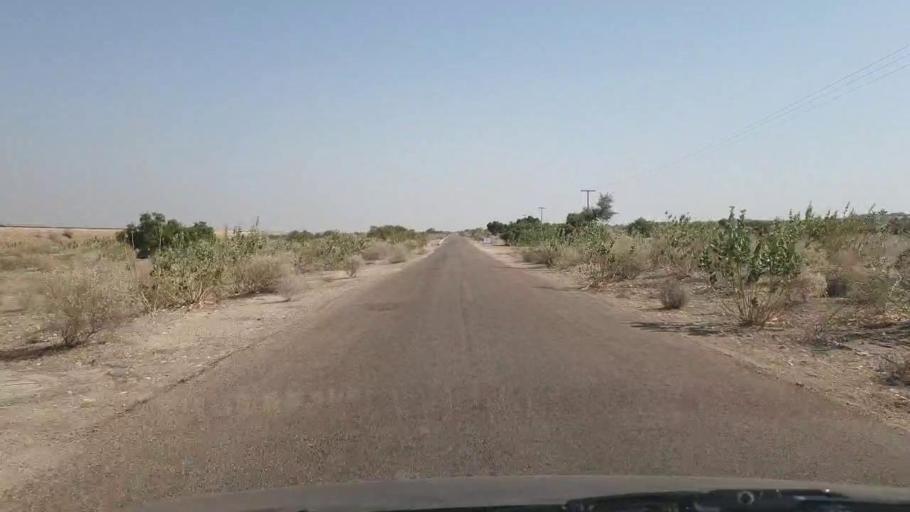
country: PK
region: Sindh
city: Chor
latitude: 25.5456
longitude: 69.8672
